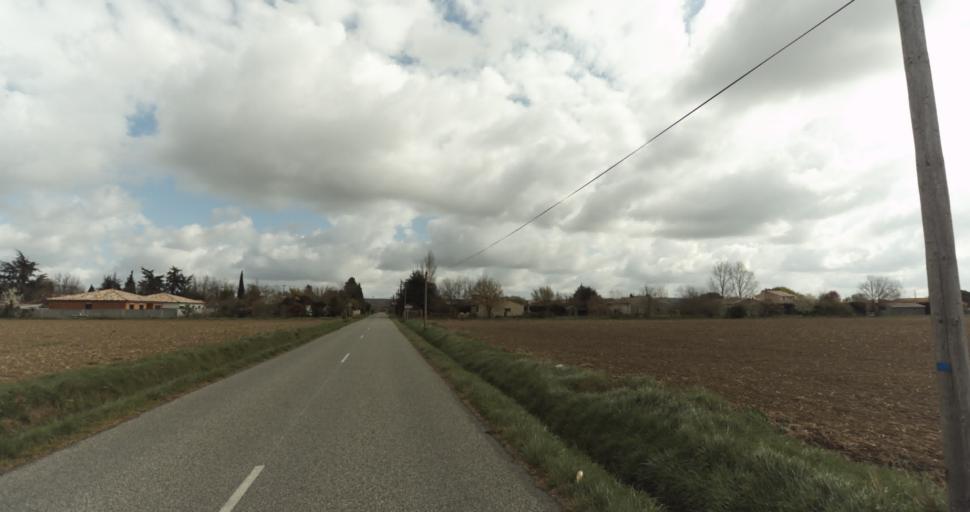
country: FR
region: Midi-Pyrenees
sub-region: Departement de la Haute-Garonne
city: Auterive
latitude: 43.3405
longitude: 1.4633
